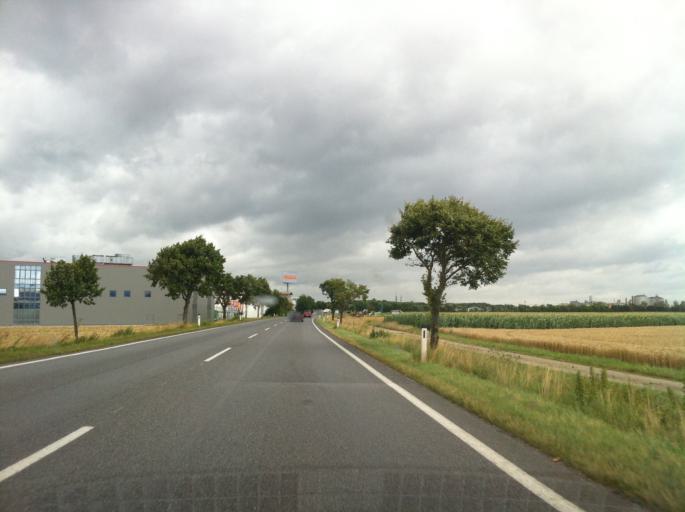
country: AT
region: Lower Austria
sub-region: Politischer Bezirk Tulln
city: Langenrohr
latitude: 48.3152
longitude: 16.0174
